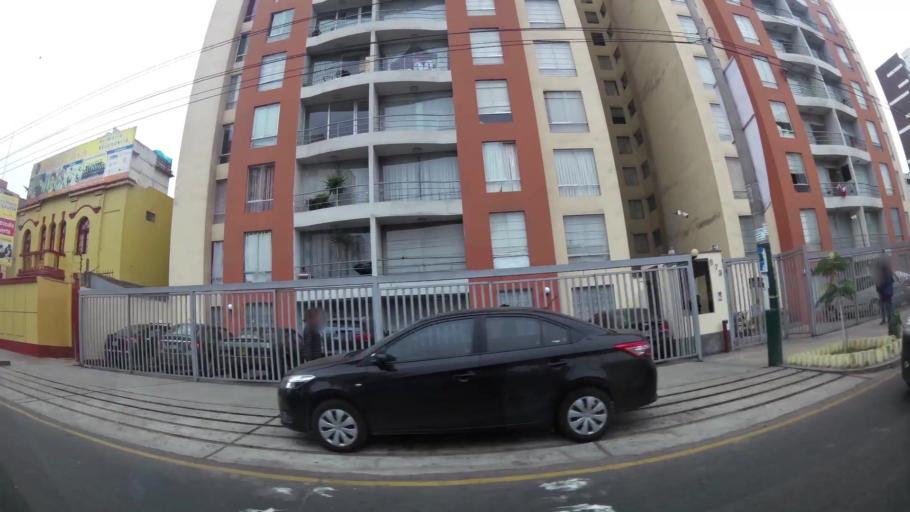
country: PE
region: Lima
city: Lima
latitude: -12.0690
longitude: -77.0486
